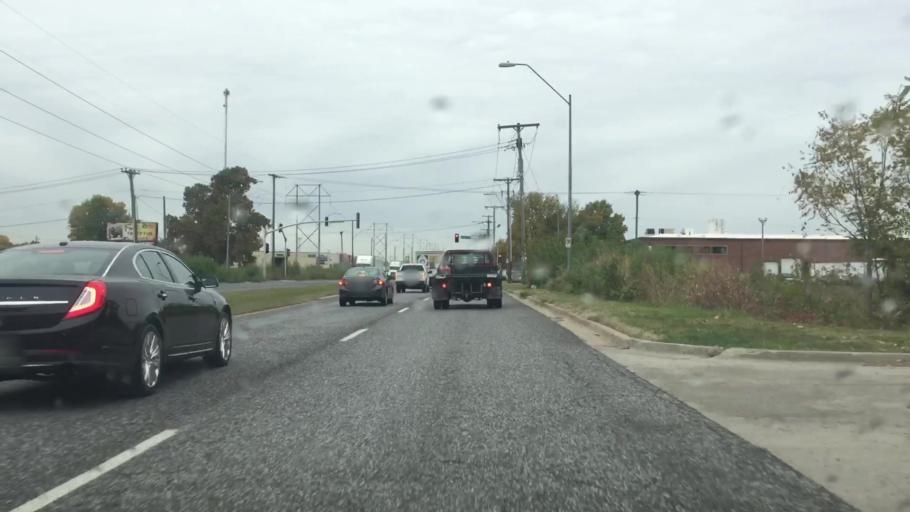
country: US
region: Missouri
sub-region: Clay County
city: North Kansas City
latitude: 39.1306
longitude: -94.5129
